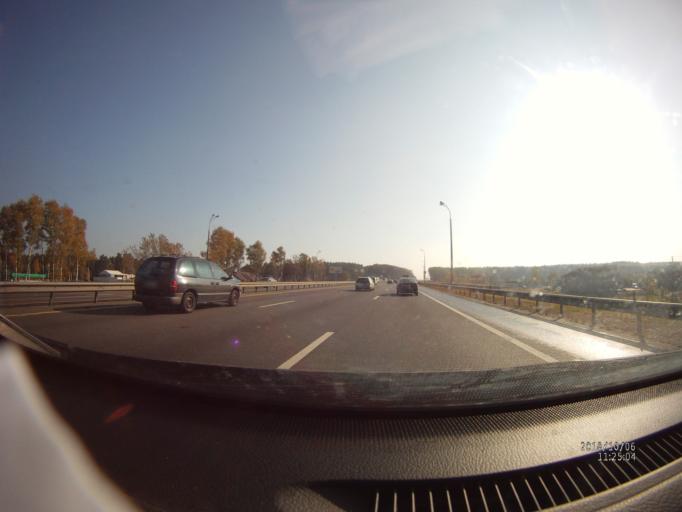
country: BY
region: Minsk
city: Bal'shavik
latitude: 53.9694
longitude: 27.5987
